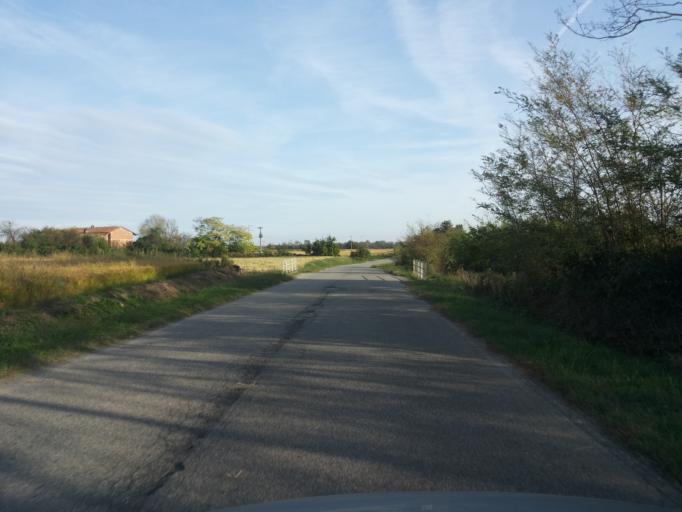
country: IT
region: Piedmont
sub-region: Provincia di Vercelli
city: Carisio
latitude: 45.4380
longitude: 8.1626
